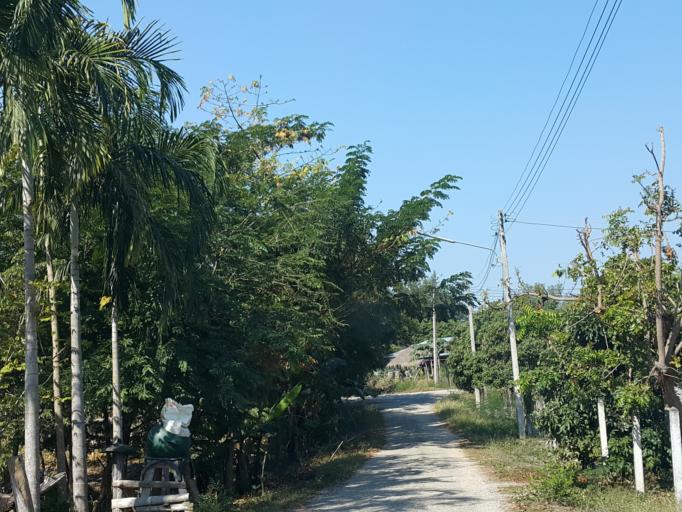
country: TH
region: Sukhothai
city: Thung Saliam
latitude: 17.3448
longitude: 99.4366
